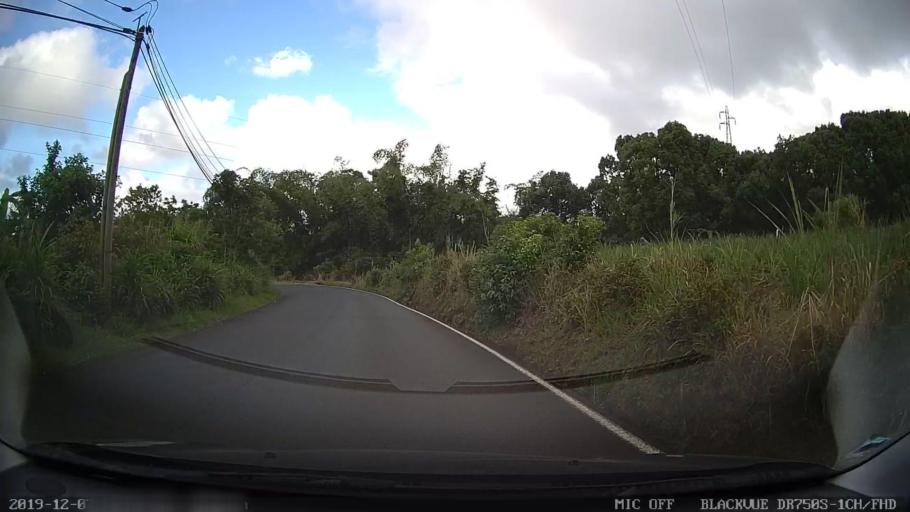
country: RE
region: Reunion
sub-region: Reunion
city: Sainte-Marie
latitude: -20.9394
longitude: 55.5350
